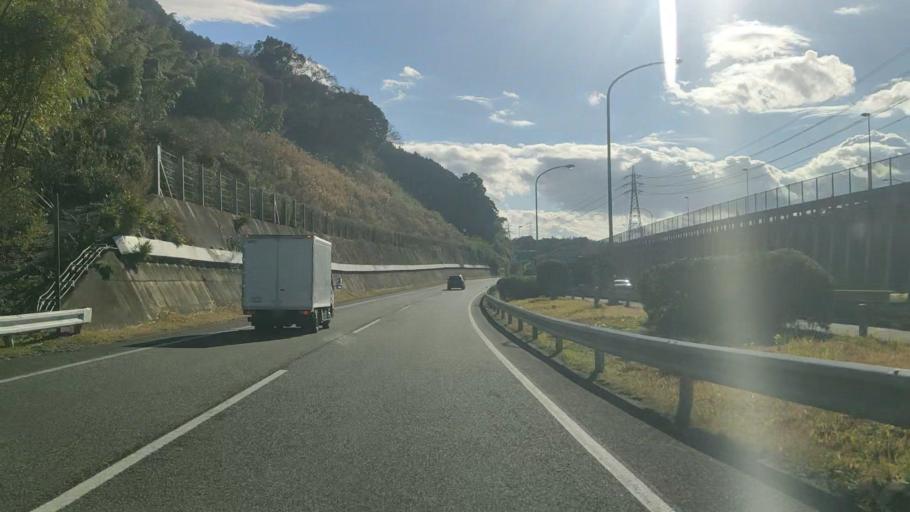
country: JP
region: Fukuoka
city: Kitakyushu
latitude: 33.8457
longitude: 130.7665
